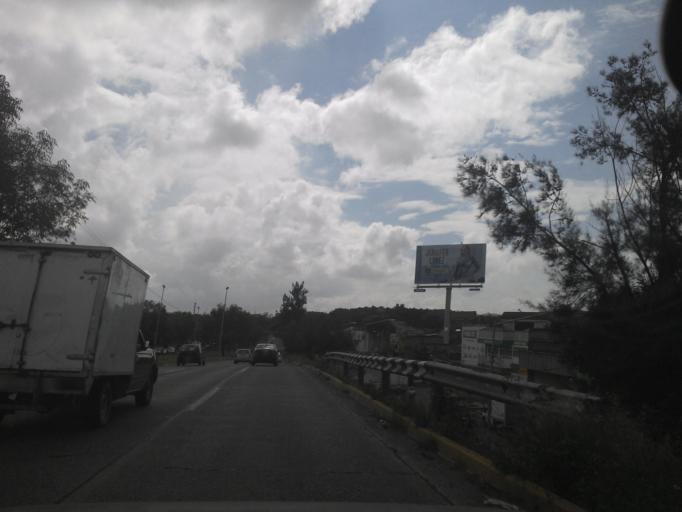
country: MX
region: Jalisco
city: Guadalajara
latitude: 20.6419
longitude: -103.3517
